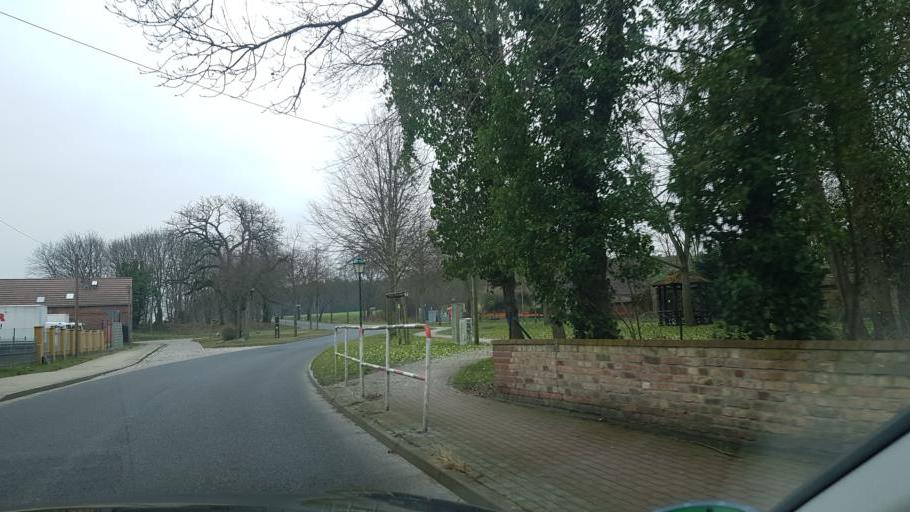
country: DE
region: Brandenburg
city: Rangsdorf
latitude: 52.3077
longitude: 13.4822
